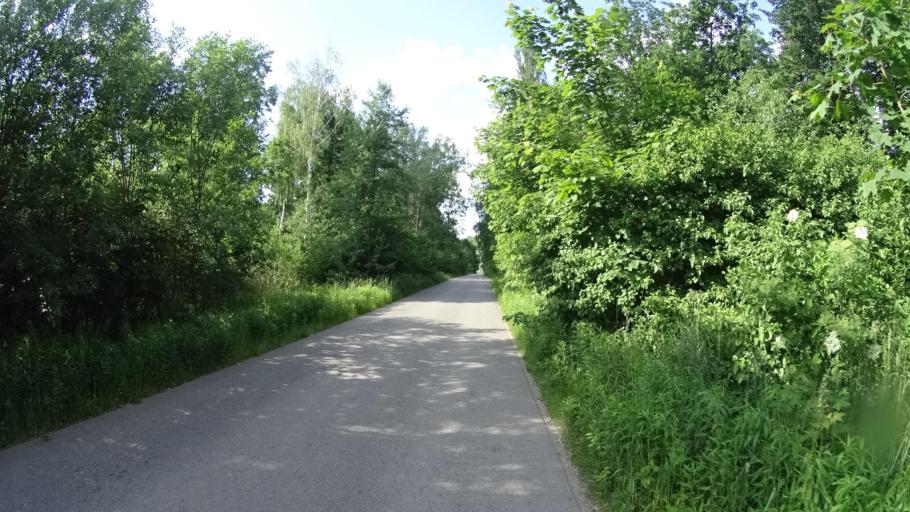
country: PL
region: Masovian Voivodeship
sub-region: Powiat pruszkowski
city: Nadarzyn
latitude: 52.0724
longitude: 20.8188
